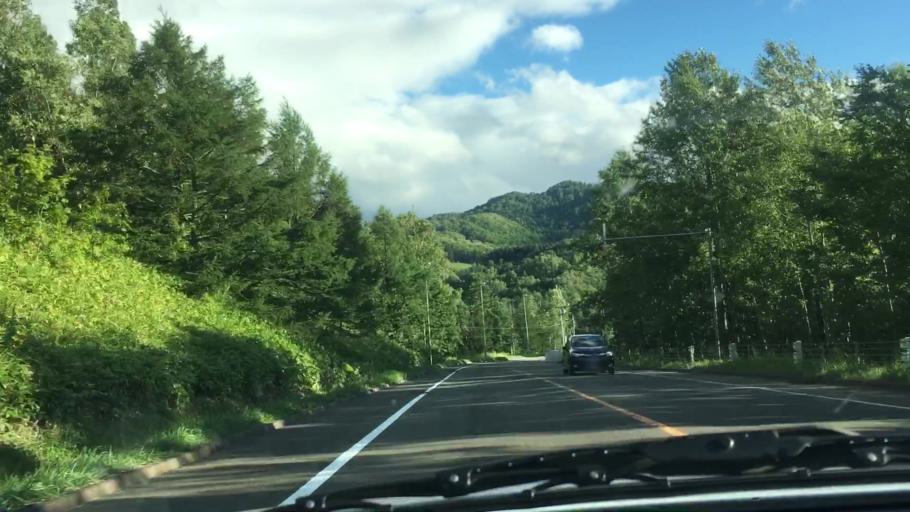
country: JP
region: Hokkaido
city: Shimo-furano
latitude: 43.1261
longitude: 142.6777
